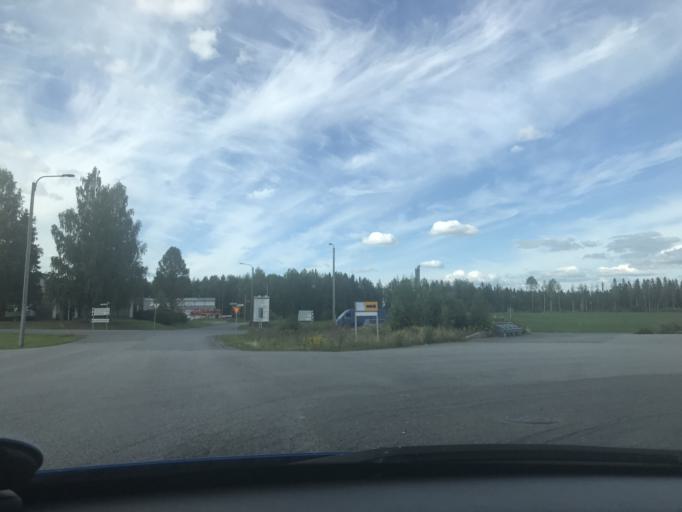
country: FI
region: Southern Ostrobothnia
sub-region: Kuusiokunnat
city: Alavus
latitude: 62.5923
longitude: 23.6036
